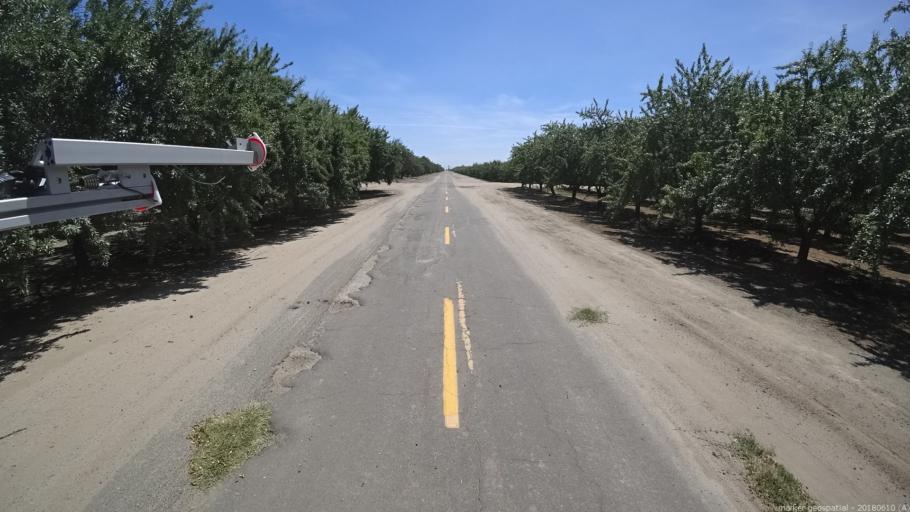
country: US
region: California
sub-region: Madera County
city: Chowchilla
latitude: 37.0398
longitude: -120.3928
